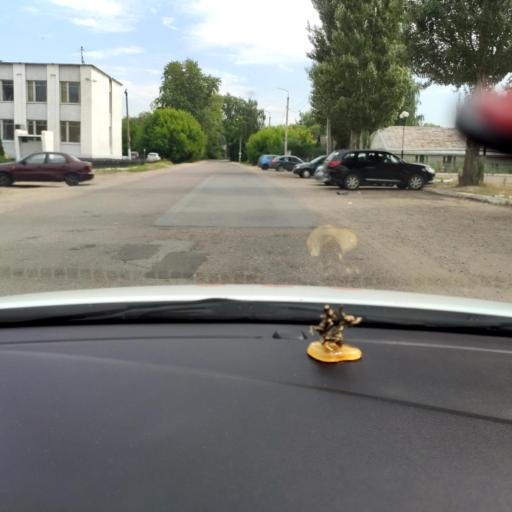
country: RU
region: Tatarstan
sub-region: Zelenodol'skiy Rayon
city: Zelenodolsk
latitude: 55.8412
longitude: 48.5607
